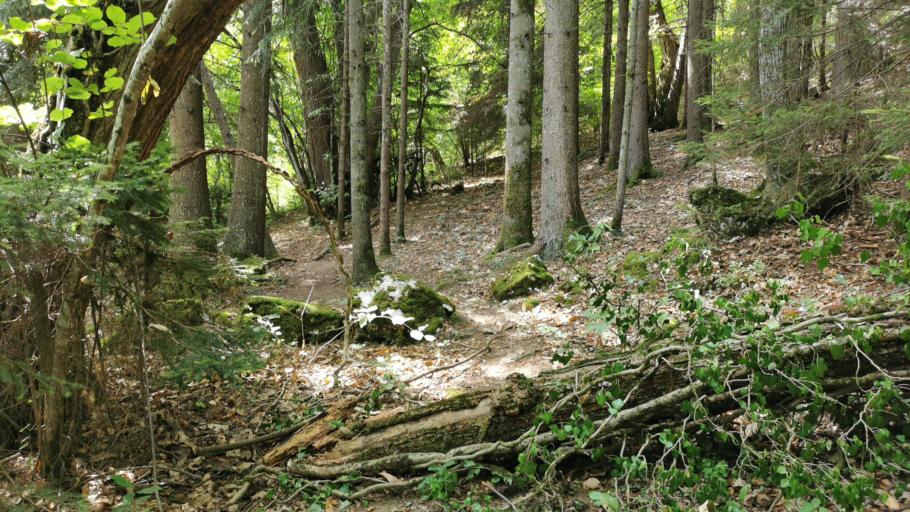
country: FR
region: Rhone-Alpes
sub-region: Departement de la Haute-Savoie
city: Sevrier
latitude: 45.8706
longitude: 6.1375
